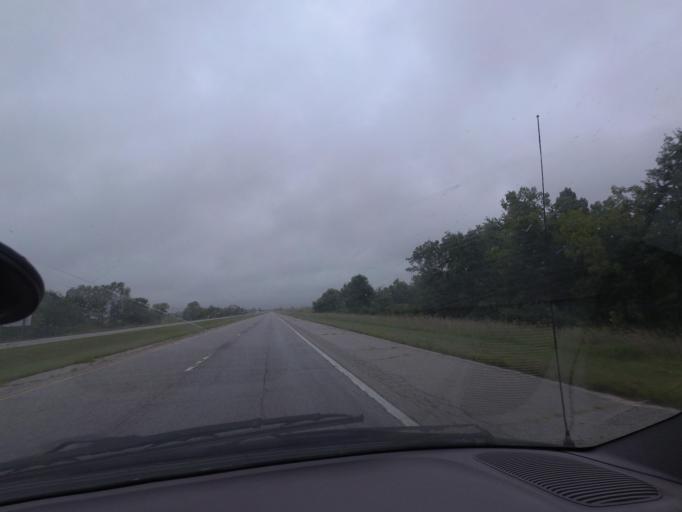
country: US
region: Illinois
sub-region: Pike County
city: Pittsfield
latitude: 39.6725
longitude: -90.8503
